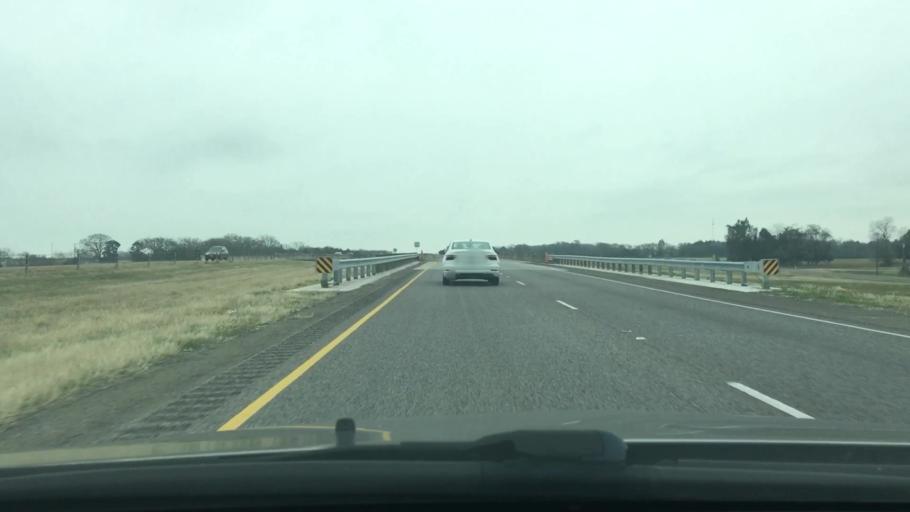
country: US
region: Texas
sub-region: Freestone County
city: Fairfield
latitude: 31.7731
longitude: -96.2237
